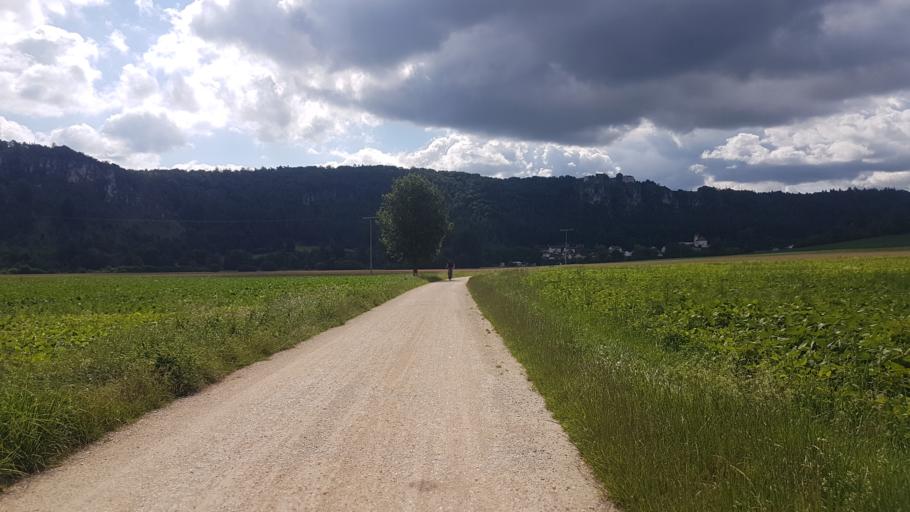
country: DE
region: Bavaria
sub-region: Upper Bavaria
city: Bohmfeld
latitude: 48.9339
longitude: 11.3664
